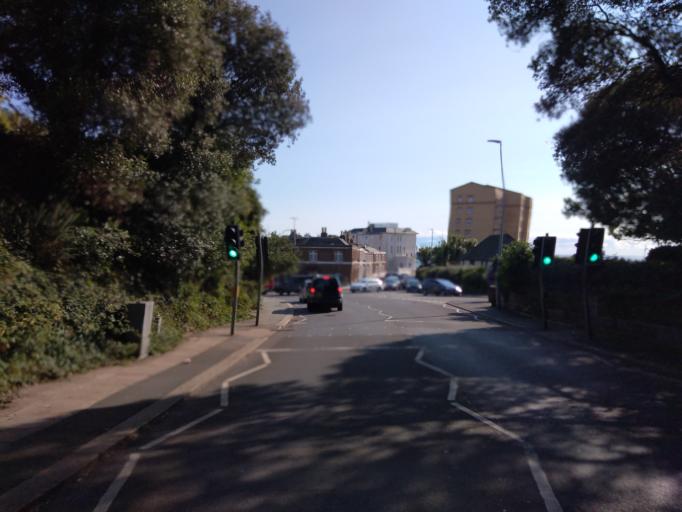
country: GB
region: England
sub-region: East Sussex
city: Hastings
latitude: 50.8554
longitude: 0.5718
